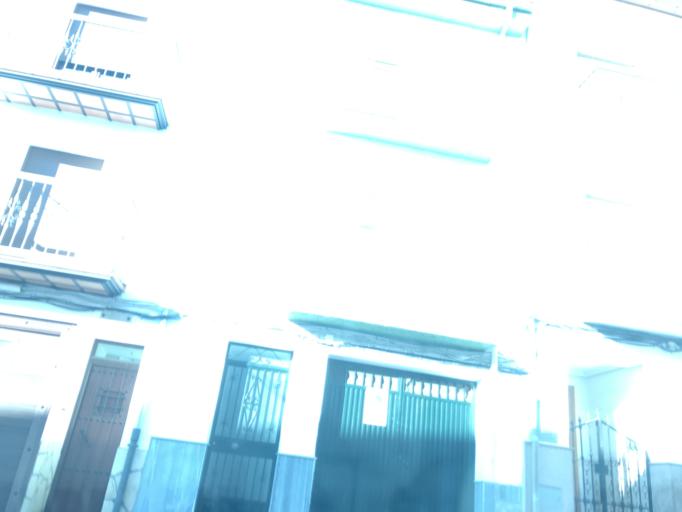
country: ES
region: Andalusia
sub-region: Provincia de Jaen
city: La Iruela
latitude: 37.9525
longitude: -2.9437
